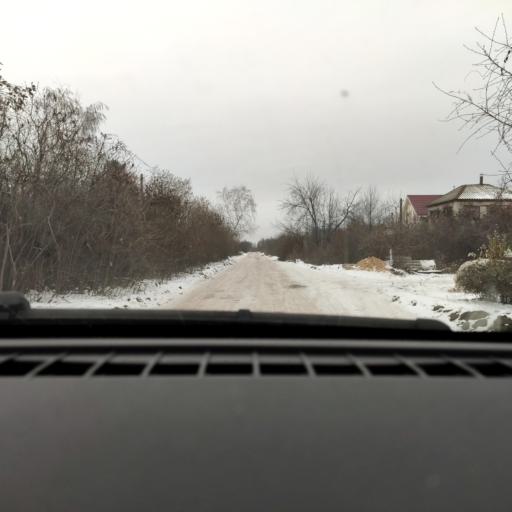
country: RU
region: Voronezj
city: Maslovka
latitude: 51.6023
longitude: 39.2836
